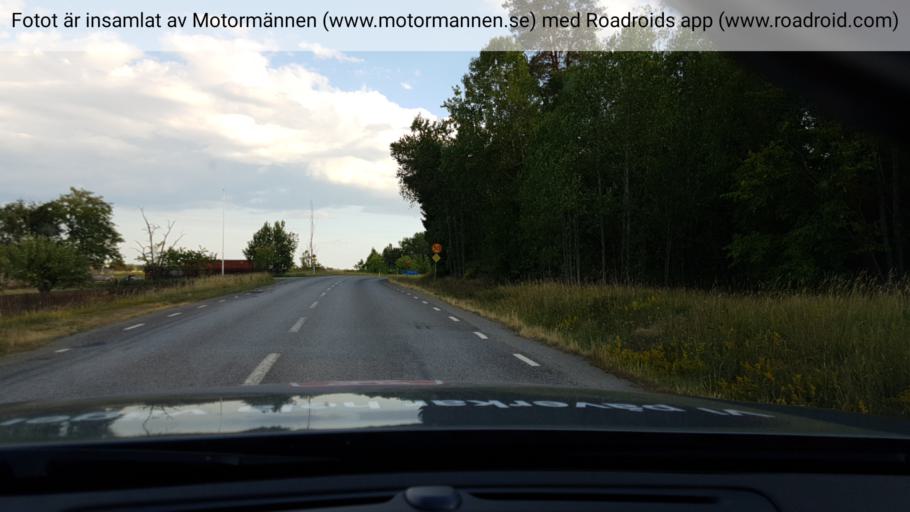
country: SE
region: Uppsala
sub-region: Enkopings Kommun
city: Irsta
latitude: 59.7723
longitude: 16.9129
